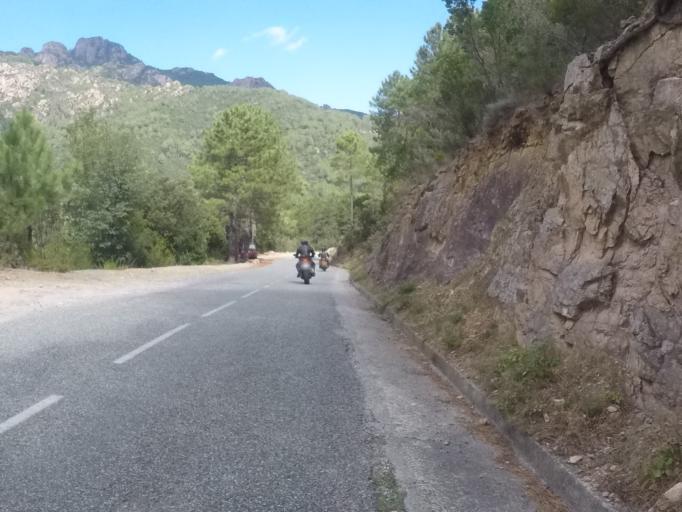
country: FR
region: Corsica
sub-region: Departement de la Corse-du-Sud
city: Sari-Solenzara
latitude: 41.8420
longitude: 9.2984
